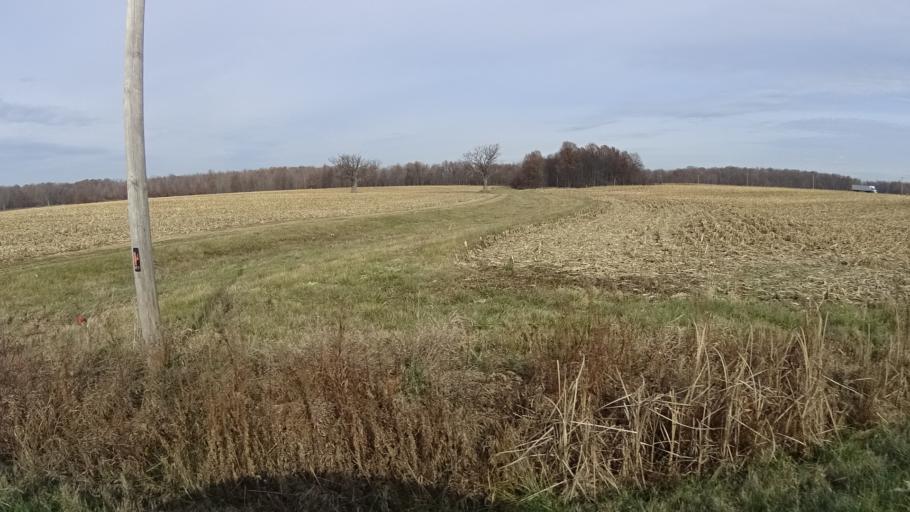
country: US
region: Ohio
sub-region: Lorain County
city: Grafton
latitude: 41.2224
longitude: -81.9863
